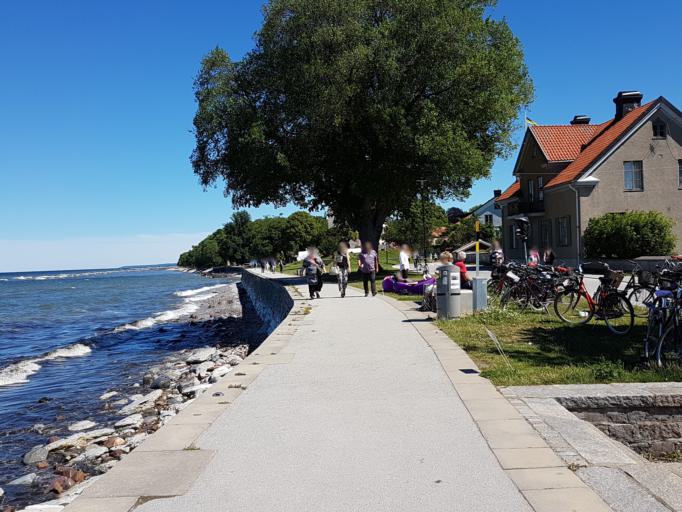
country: SE
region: Gotland
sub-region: Gotland
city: Visby
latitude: 57.6408
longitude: 18.2885
